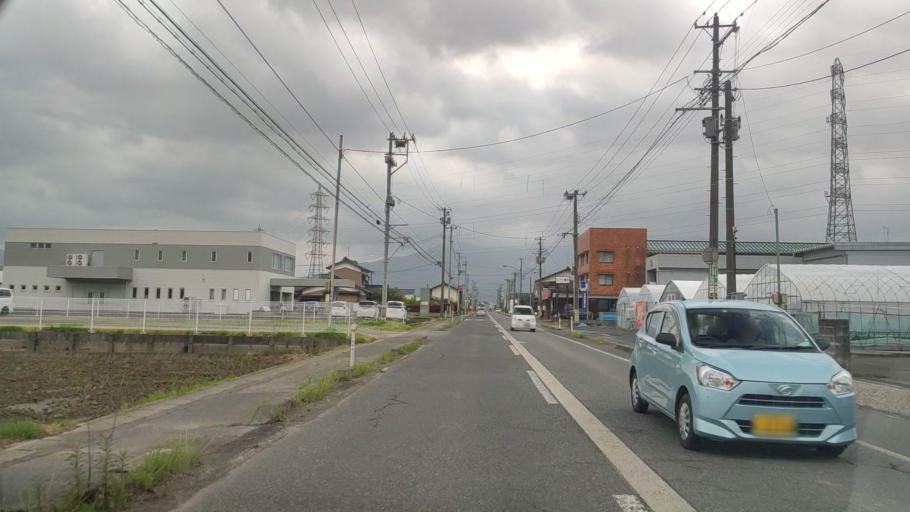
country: JP
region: Niigata
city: Gosen
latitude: 37.7346
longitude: 139.1947
